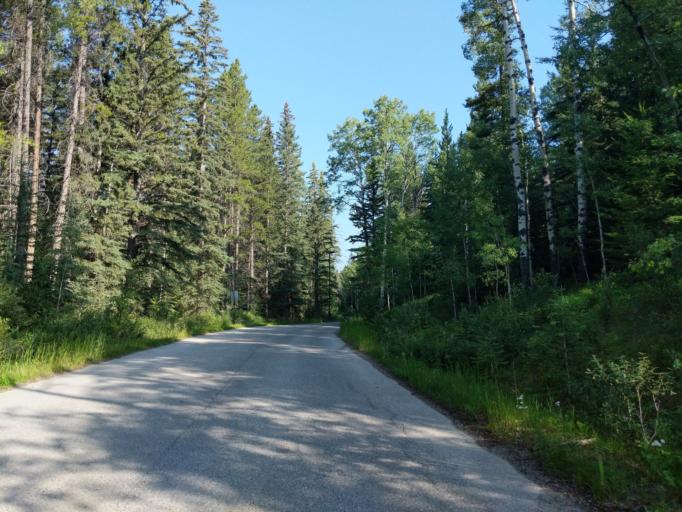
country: CA
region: Alberta
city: Canmore
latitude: 51.1014
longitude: -115.3434
